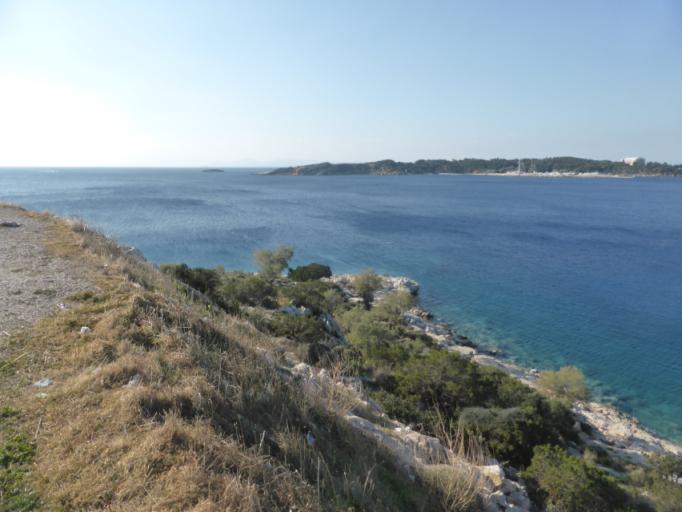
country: GR
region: Attica
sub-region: Nomarchia Anatolikis Attikis
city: Vouliagmeni
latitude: 37.8014
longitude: 23.7868
